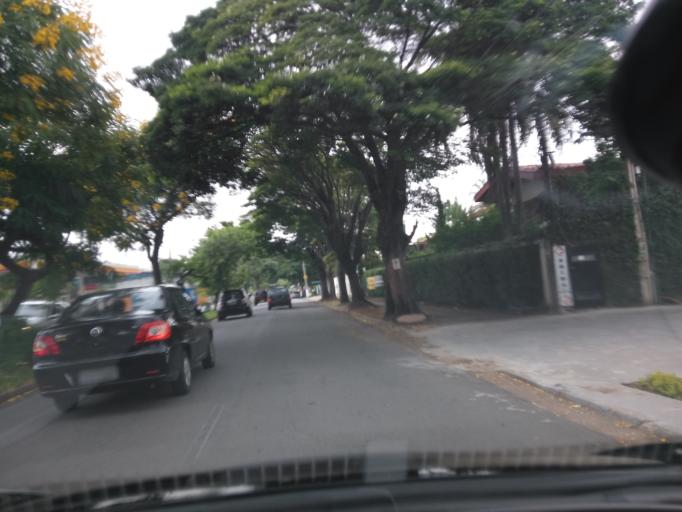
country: BR
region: Sao Paulo
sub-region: Campinas
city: Campinas
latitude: -22.8997
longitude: -47.0300
